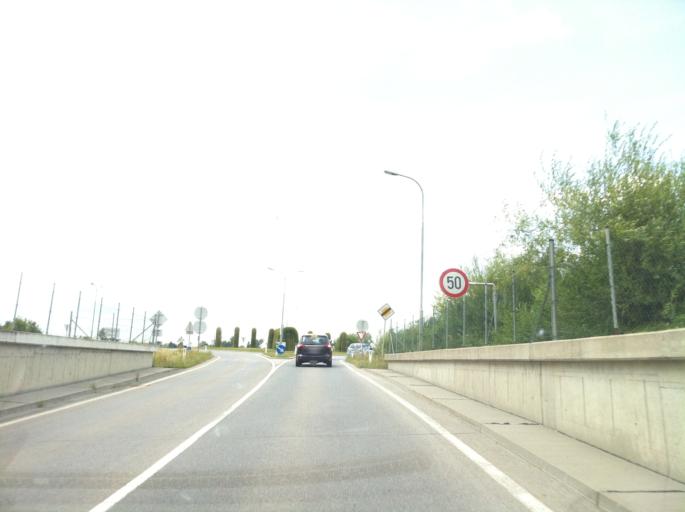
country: AT
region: Lower Austria
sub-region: Politischer Bezirk Tulln
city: Tulln
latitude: 48.2912
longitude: 16.0658
